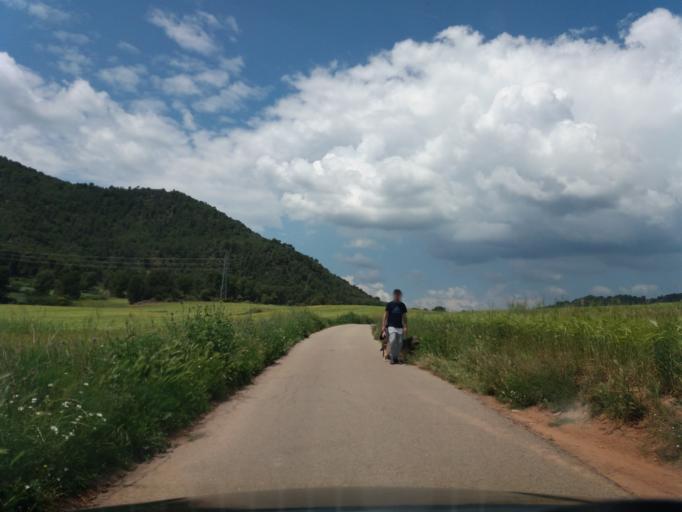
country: ES
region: Catalonia
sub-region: Provincia de Barcelona
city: Sant Joan de Vilatorrada
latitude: 41.7446
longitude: 1.7931
